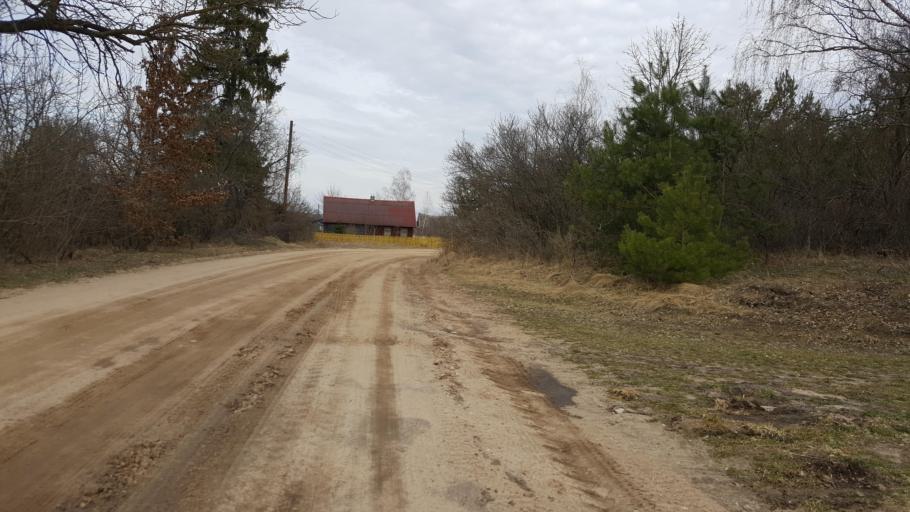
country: BY
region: Brest
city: Kamyanyets
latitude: 52.3730
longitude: 23.9813
